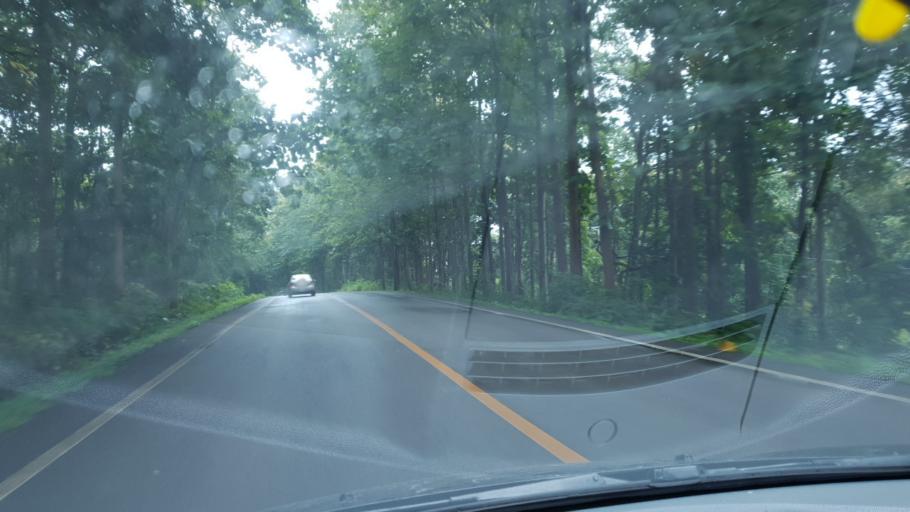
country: TH
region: Mae Hong Son
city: Pa Pae
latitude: 18.2287
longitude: 97.9445
